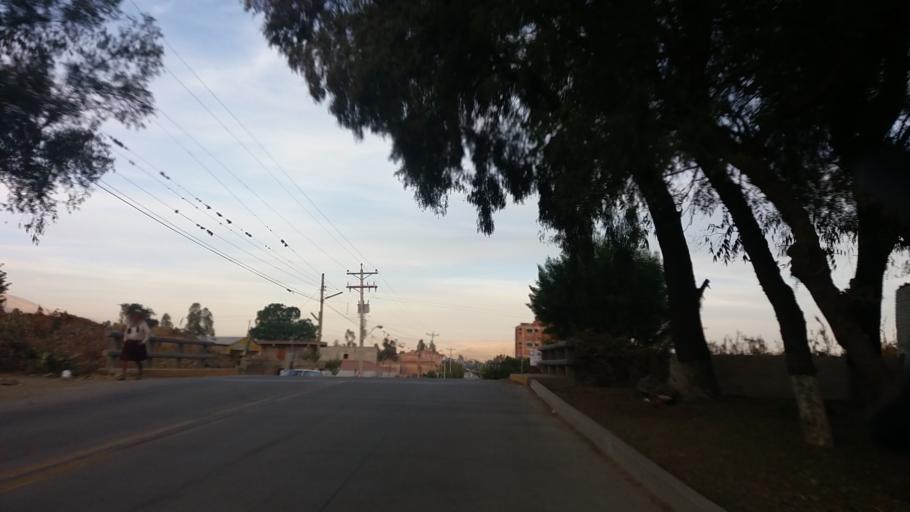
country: BO
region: Cochabamba
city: Cochabamba
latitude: -17.3645
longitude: -66.2197
